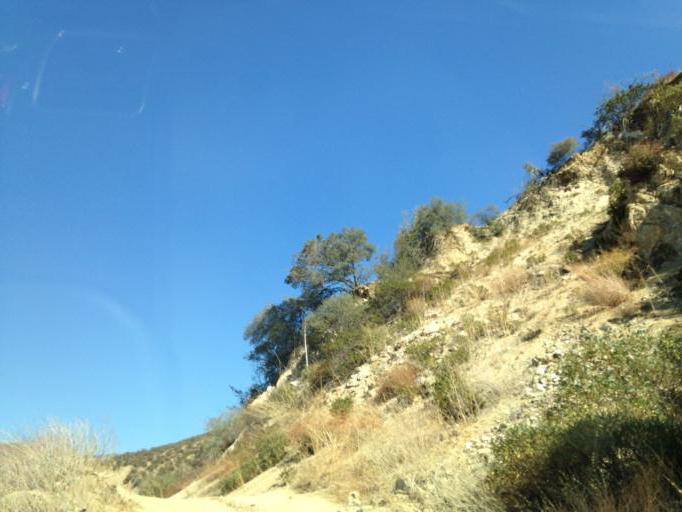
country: US
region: California
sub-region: San Bernardino County
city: Mentone
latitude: 34.1211
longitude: -117.1106
